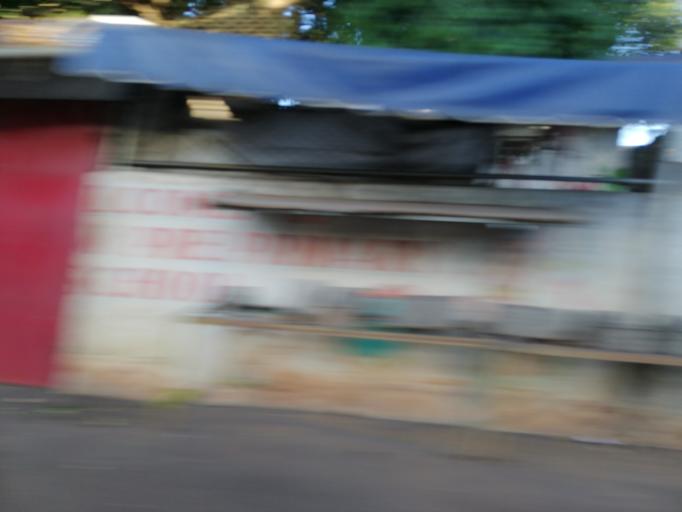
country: MU
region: Pamplemousses
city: Terre Rouge
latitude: -20.1242
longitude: 57.5317
